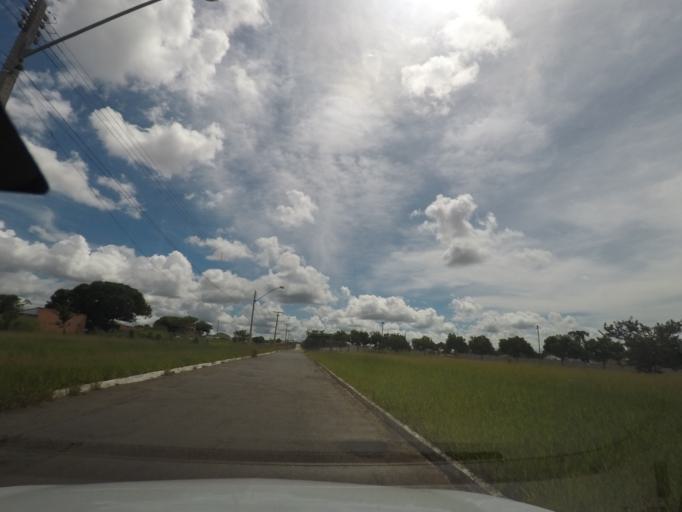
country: BR
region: Goias
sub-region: Goiania
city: Goiania
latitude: -16.7533
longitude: -49.3396
